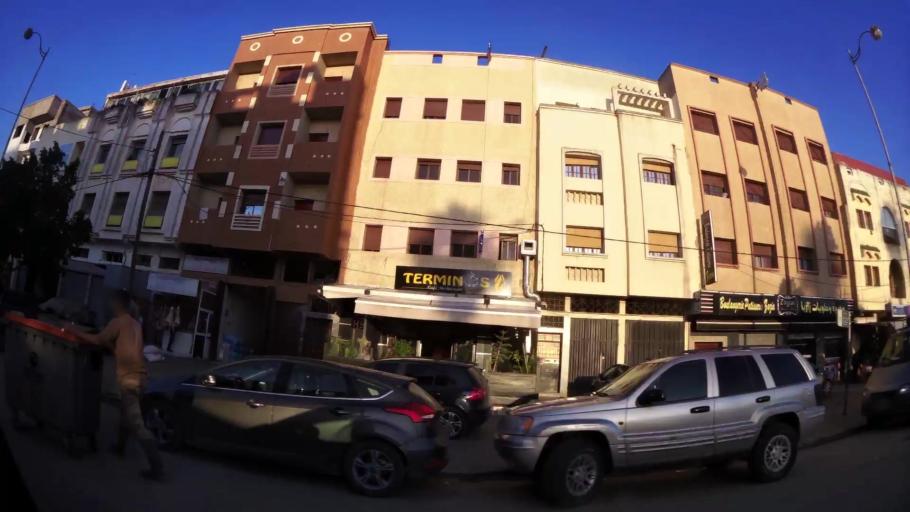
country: MA
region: Chaouia-Ouardigha
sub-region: Settat Province
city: Settat
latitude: 32.9959
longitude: -7.6172
